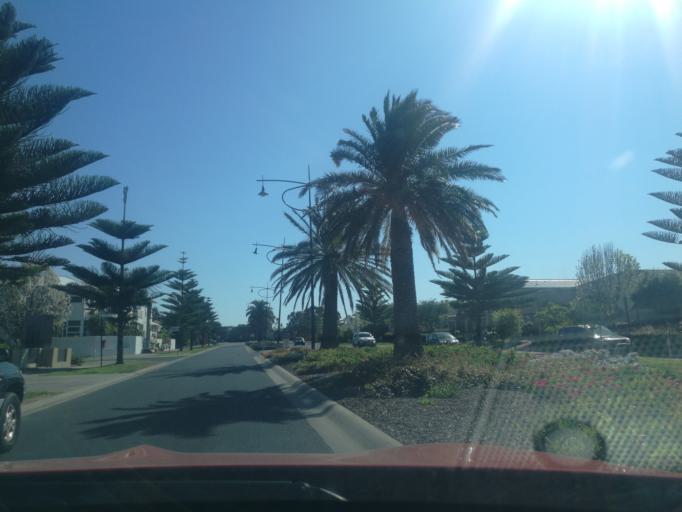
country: AU
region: Victoria
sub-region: Wyndham
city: Williams Landing
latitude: -37.8874
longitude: 144.7411
